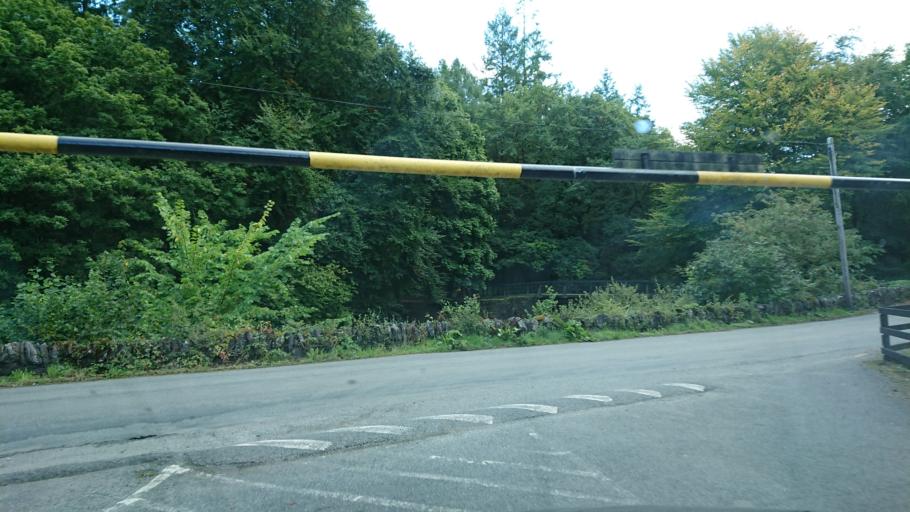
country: IE
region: Munster
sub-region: Waterford
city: Dungarvan
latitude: 52.1278
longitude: -7.6875
